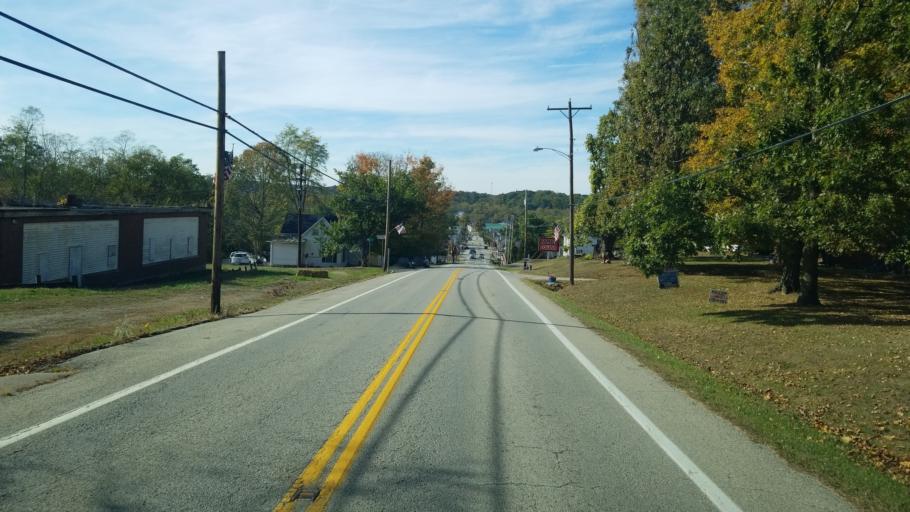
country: US
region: Ohio
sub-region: Clinton County
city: Blanchester
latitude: 39.3993
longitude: -83.9773
